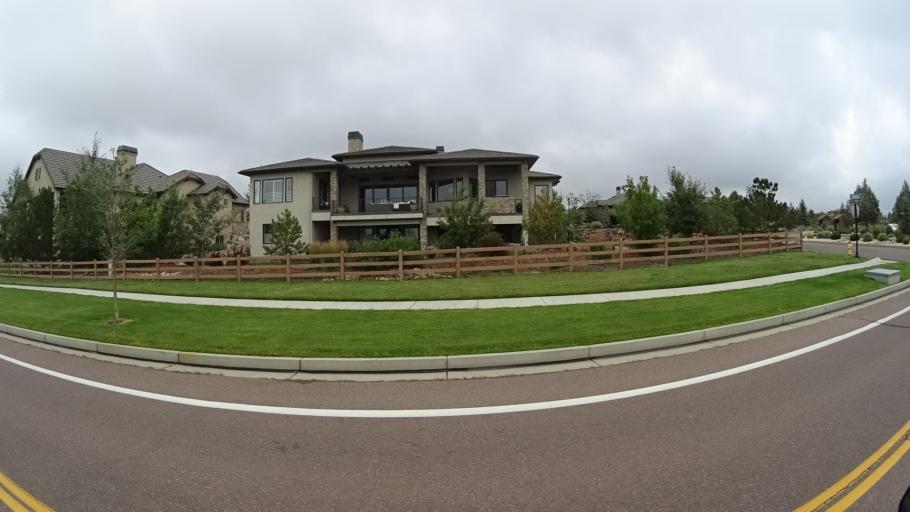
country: US
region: Colorado
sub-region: El Paso County
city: Gleneagle
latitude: 39.0276
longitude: -104.7889
